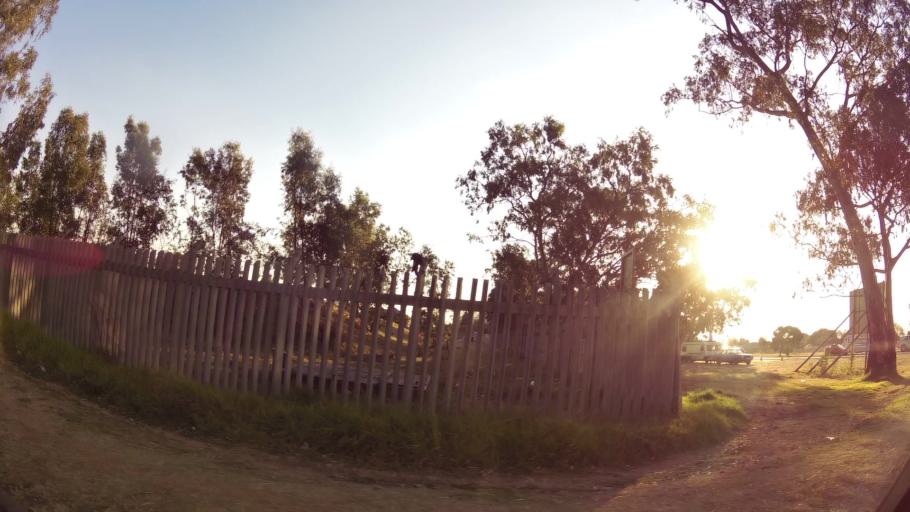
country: ZA
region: Gauteng
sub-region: City of Johannesburg Metropolitan Municipality
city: Johannesburg
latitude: -26.2569
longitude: 28.0074
